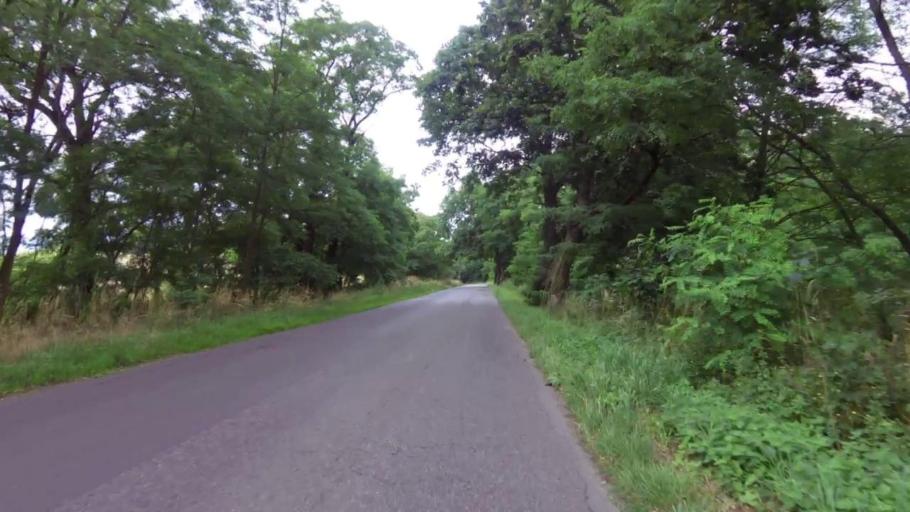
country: PL
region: West Pomeranian Voivodeship
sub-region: Powiat gryfinski
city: Moryn
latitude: 52.8660
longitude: 14.3840
